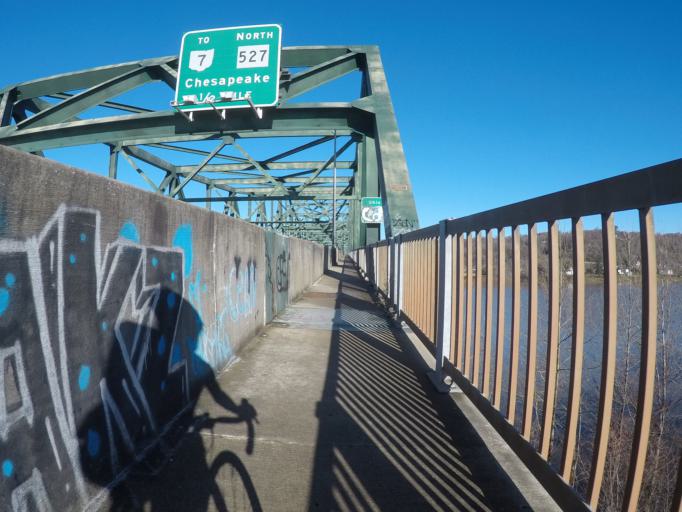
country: US
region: West Virginia
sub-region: Cabell County
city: Huntington
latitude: 38.4225
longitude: -82.4506
